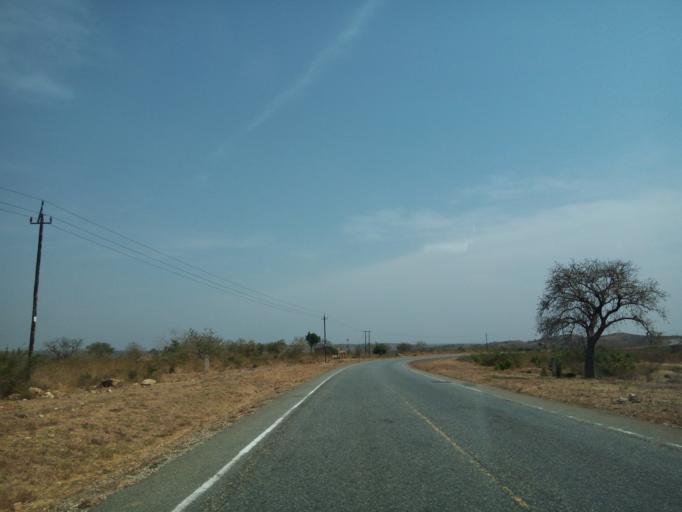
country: UG
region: Northern Region
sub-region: Nebbi District
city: Nebbi
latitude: 2.4442
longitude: 31.2536
